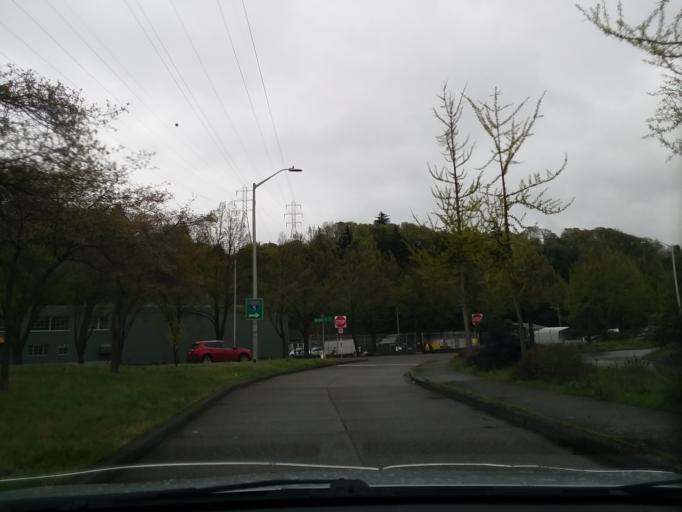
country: US
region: Washington
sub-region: King County
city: Seattle
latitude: 47.5648
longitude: -122.3233
